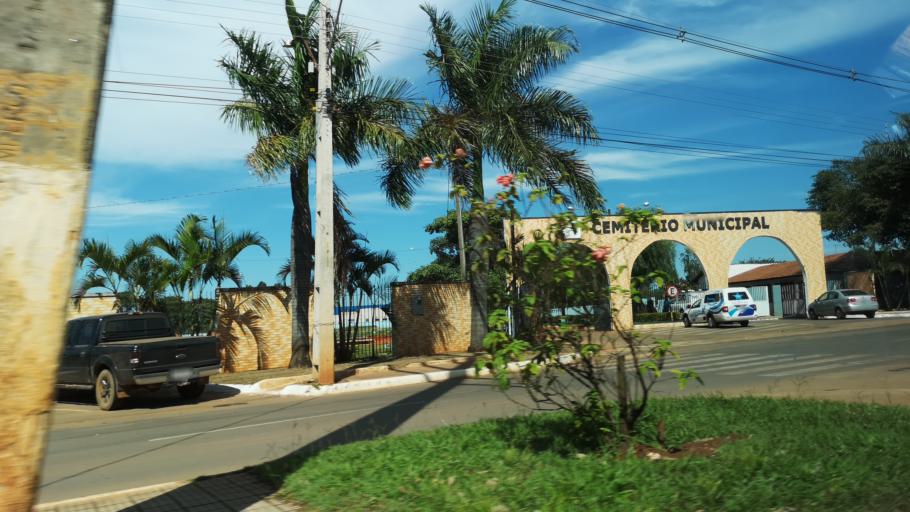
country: BR
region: Goias
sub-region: Senador Canedo
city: Senador Canedo
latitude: -16.7035
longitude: -49.1072
